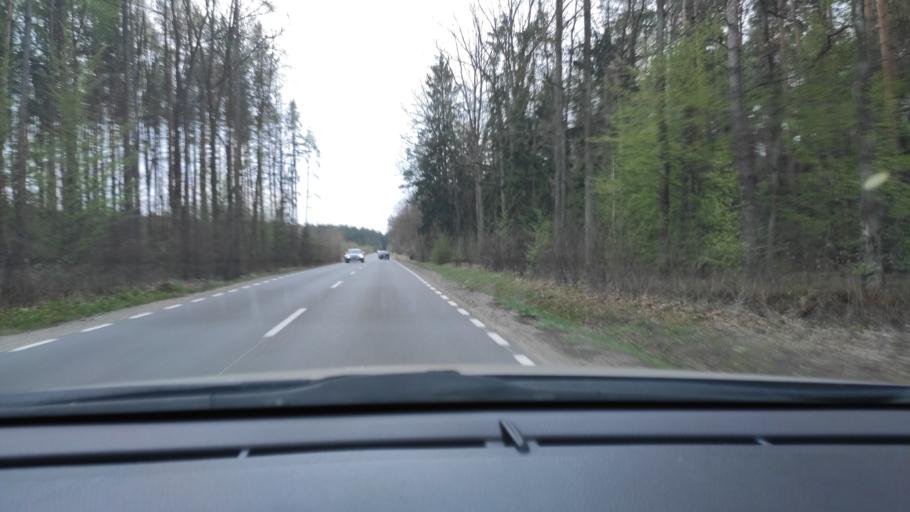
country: PL
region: Masovian Voivodeship
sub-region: Powiat radomski
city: Pionki
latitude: 51.4989
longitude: 21.4270
